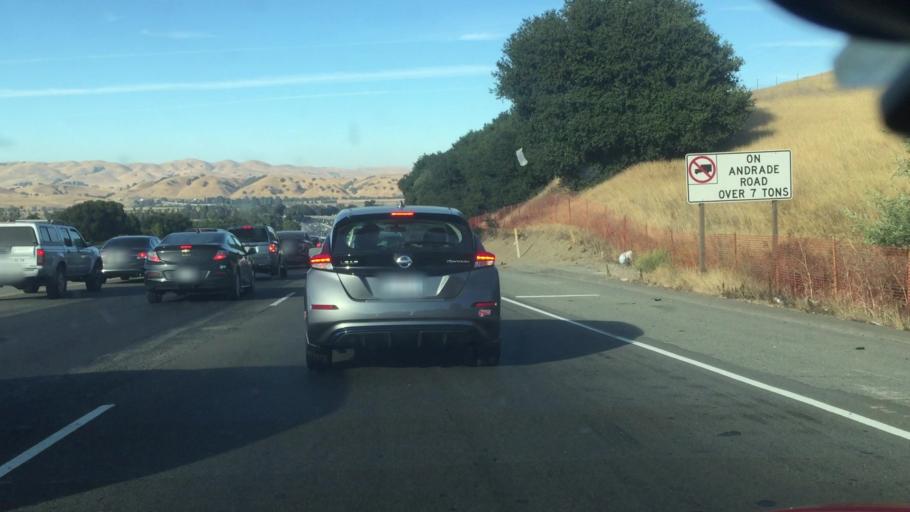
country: US
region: California
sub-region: Alameda County
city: Fremont
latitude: 37.5676
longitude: -121.8948
